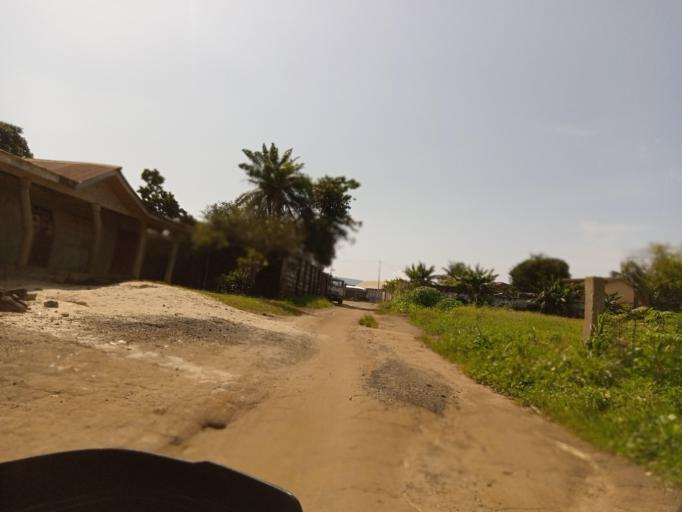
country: SL
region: Northern Province
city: Masoyila
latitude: 8.6104
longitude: -13.2046
